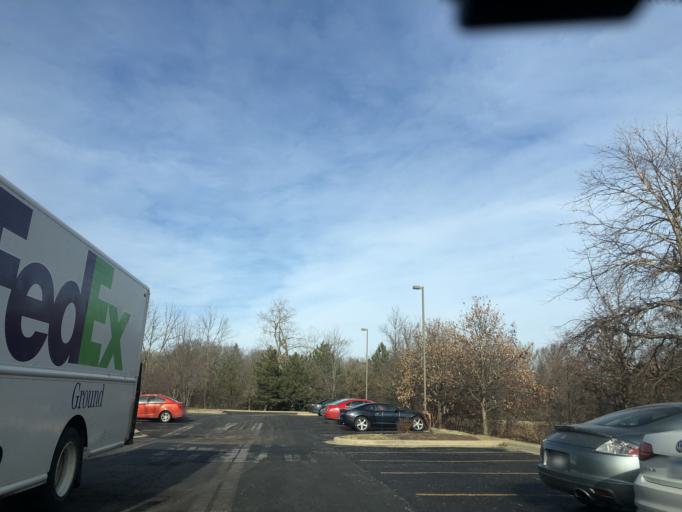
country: US
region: Illinois
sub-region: DuPage County
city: Darien
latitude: 41.7207
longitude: -88.0095
